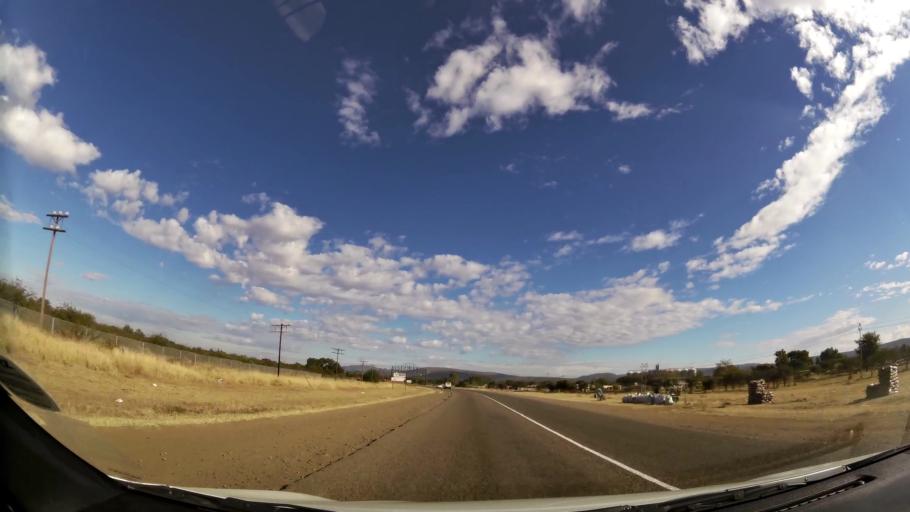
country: ZA
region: Limpopo
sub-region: Waterberg District Municipality
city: Bela-Bela
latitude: -24.8920
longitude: 28.3091
